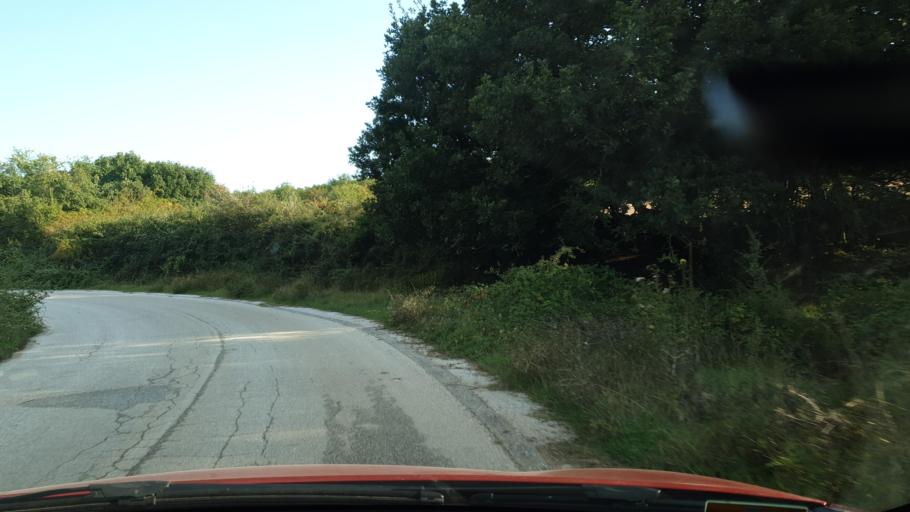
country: GR
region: Central Macedonia
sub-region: Nomos Chalkidikis
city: Galatista
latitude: 40.5069
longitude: 23.2230
